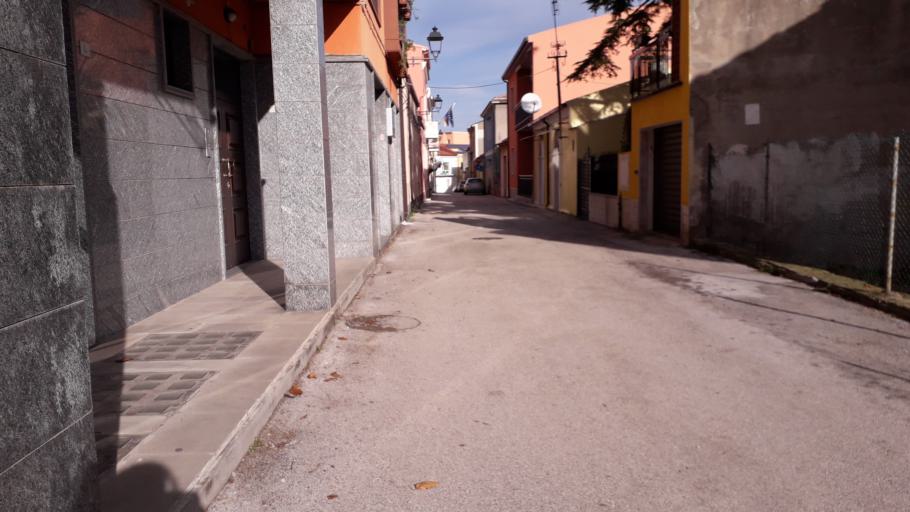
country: IT
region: Molise
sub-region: Provincia di Campobasso
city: Campomarino
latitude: 41.9566
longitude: 15.0328
